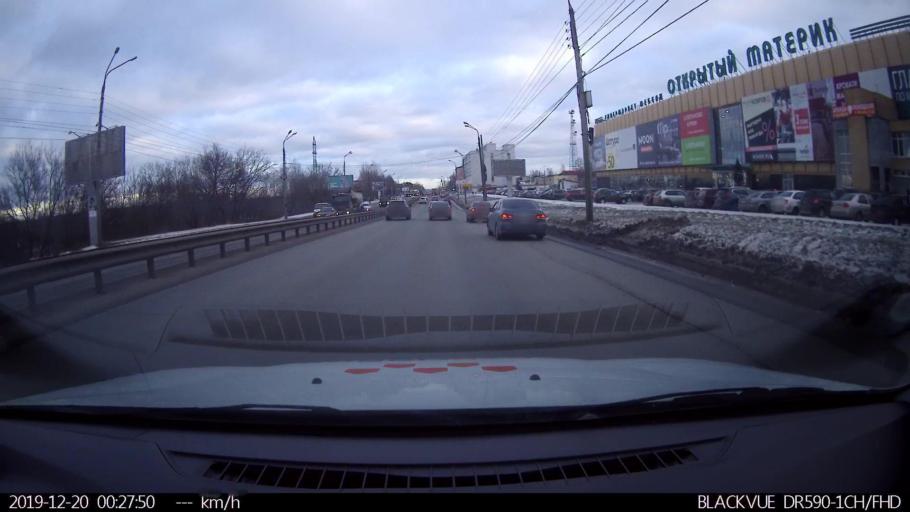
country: RU
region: Vladimir
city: Yur'yev-Pol'skiy
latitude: 56.5835
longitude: 39.5886
